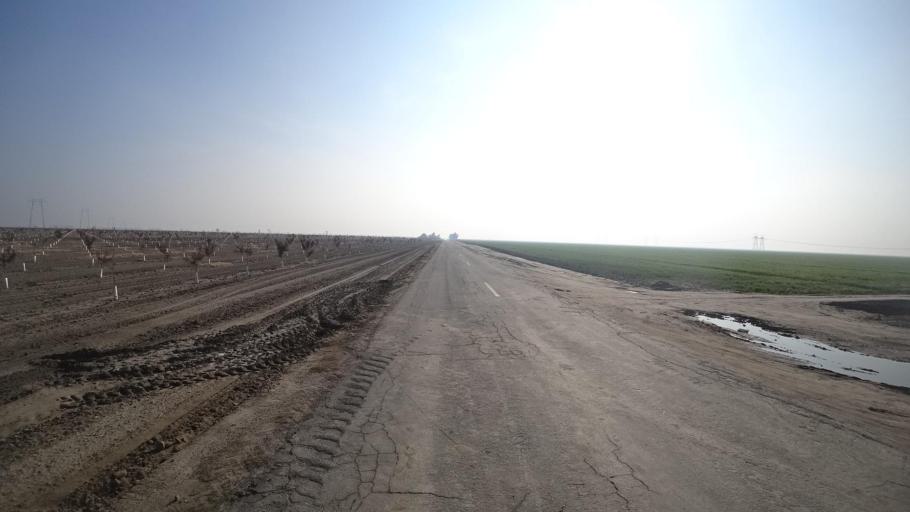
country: US
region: California
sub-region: Kern County
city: Greenfield
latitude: 35.1685
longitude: -119.0393
